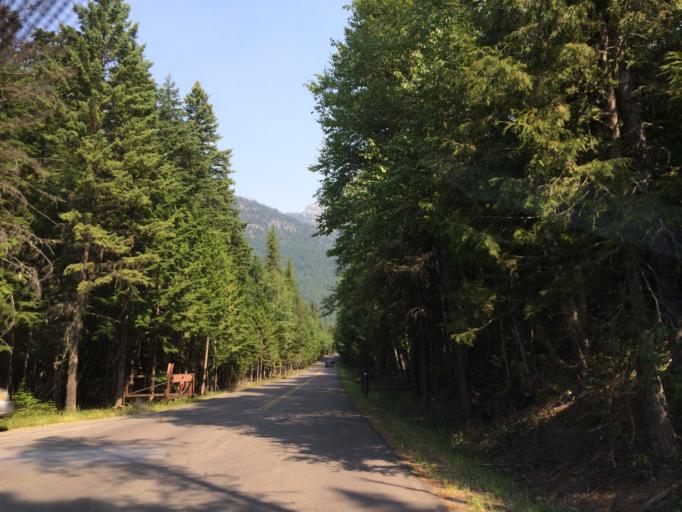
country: US
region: Montana
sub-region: Flathead County
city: Columbia Falls
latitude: 48.6349
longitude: -113.8633
